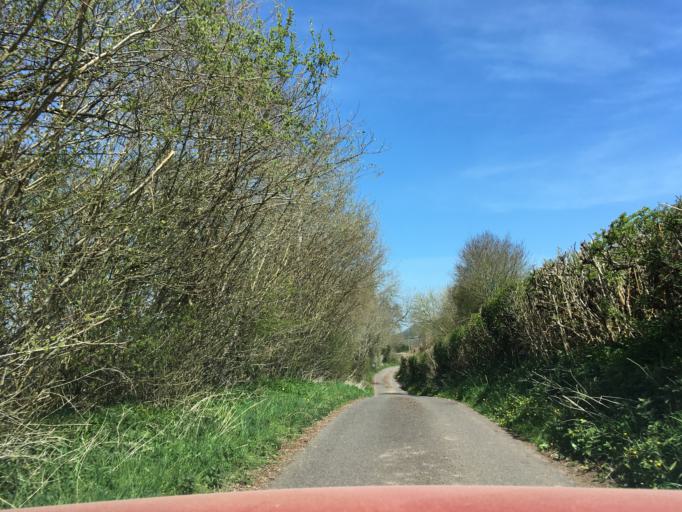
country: GB
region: Wales
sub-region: Monmouthshire
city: Llangwm
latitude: 51.6990
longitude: -2.8303
